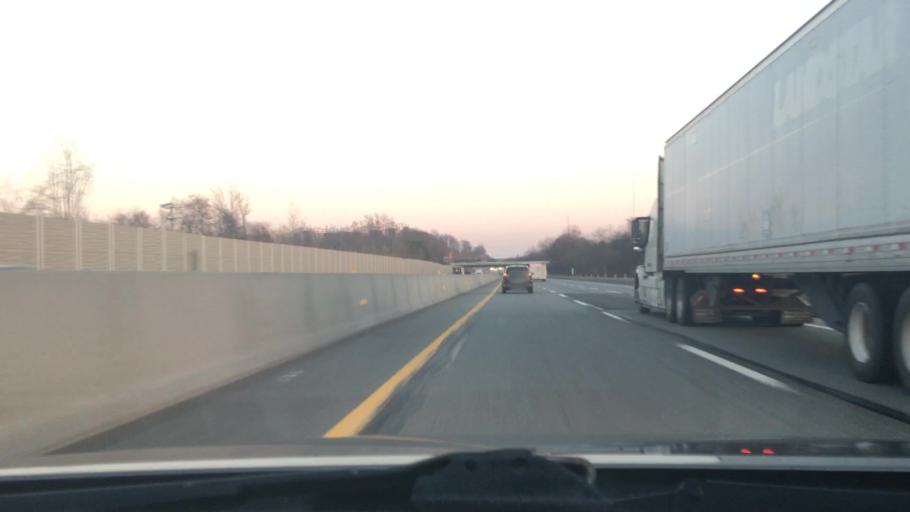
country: US
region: Pennsylvania
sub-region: Montgomery County
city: King of Prussia
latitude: 40.0914
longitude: -75.3825
